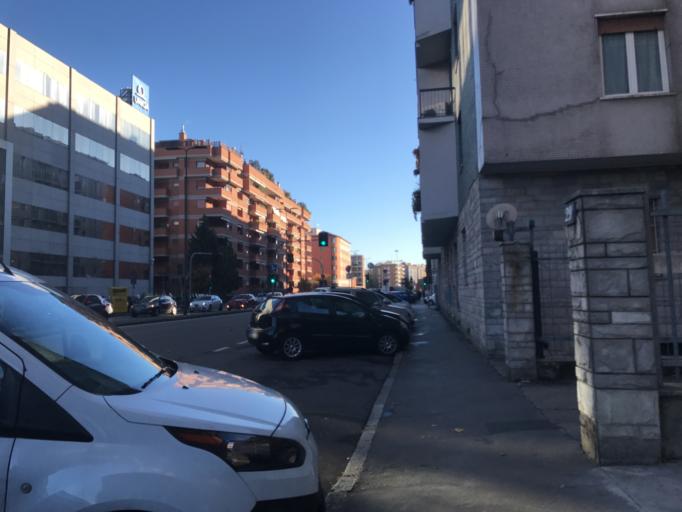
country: IT
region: Lombardy
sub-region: Citta metropolitana di Milano
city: Sesto San Giovanni
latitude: 45.4943
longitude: 9.2358
